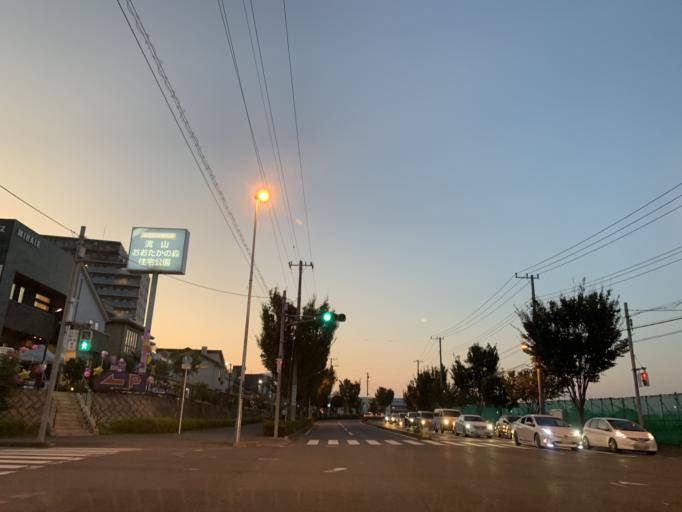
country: JP
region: Chiba
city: Nagareyama
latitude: 35.8714
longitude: 139.9213
